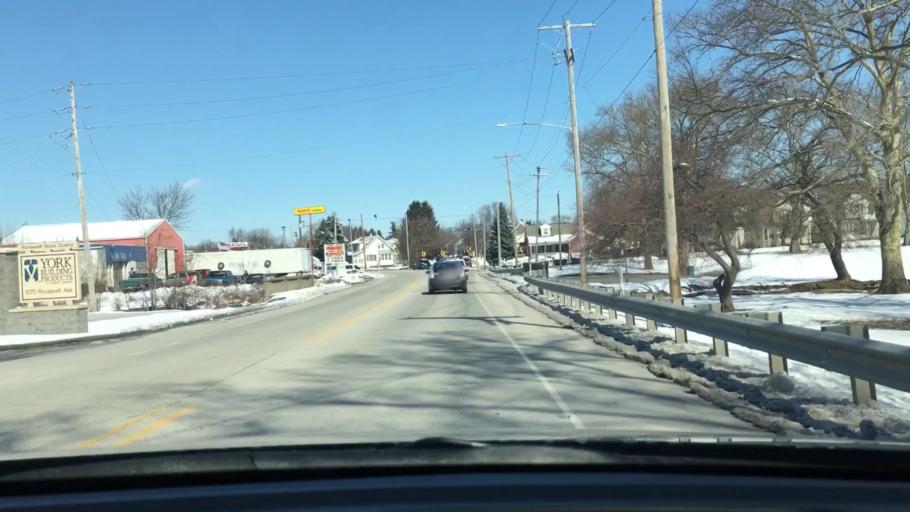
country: US
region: Pennsylvania
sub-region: York County
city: West York
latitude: 39.9696
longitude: -76.7513
